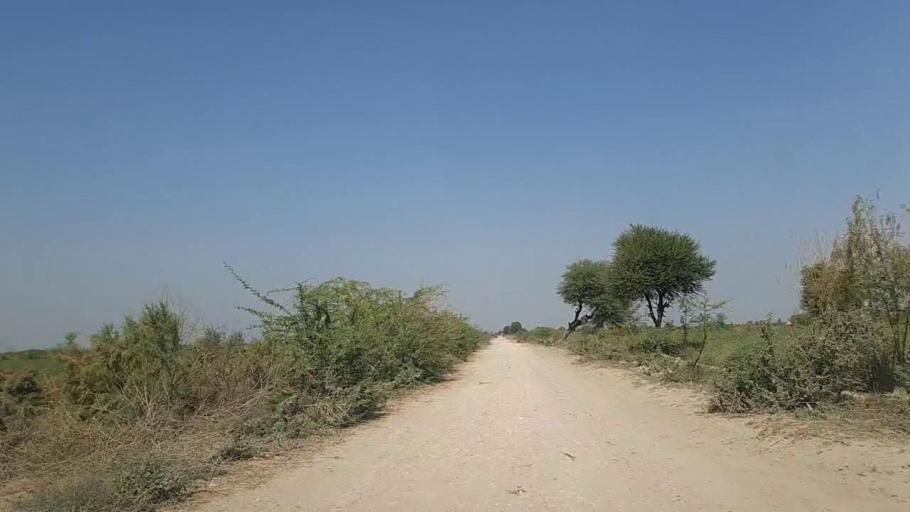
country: PK
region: Sindh
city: Samaro
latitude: 25.2037
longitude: 69.4042
